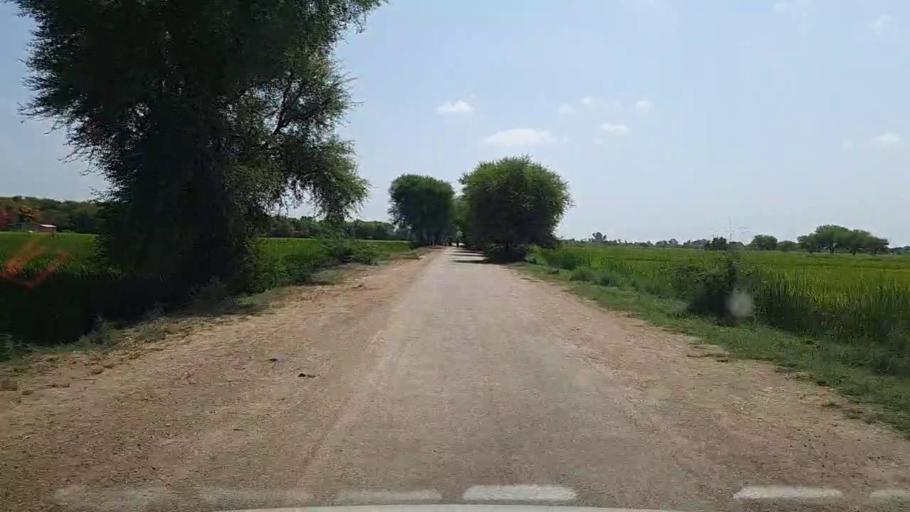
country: PK
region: Sindh
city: Kario
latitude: 24.8267
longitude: 68.7030
